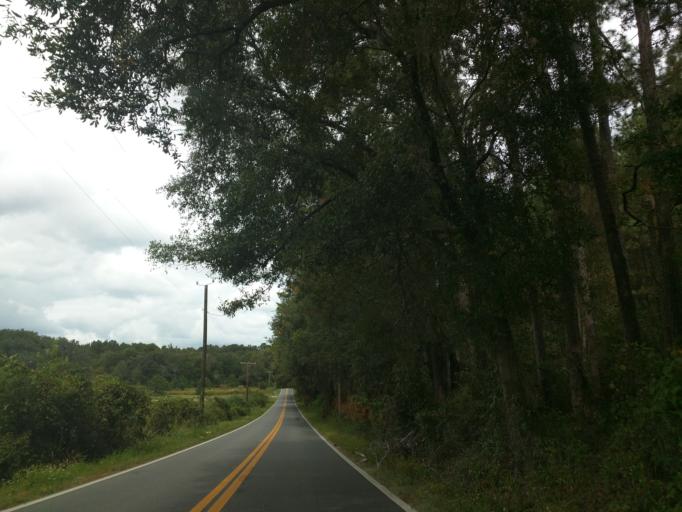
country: US
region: Florida
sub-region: Leon County
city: Tallahassee
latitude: 30.4083
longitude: -84.2102
